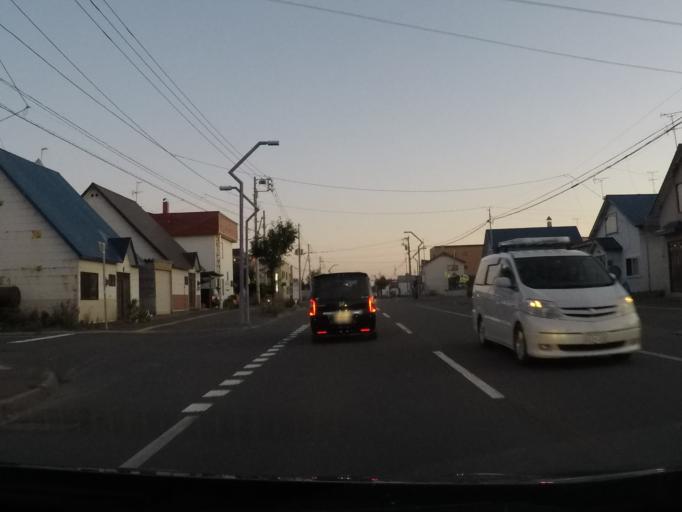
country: JP
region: Hokkaido
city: Nayoro
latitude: 44.3455
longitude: 142.4503
